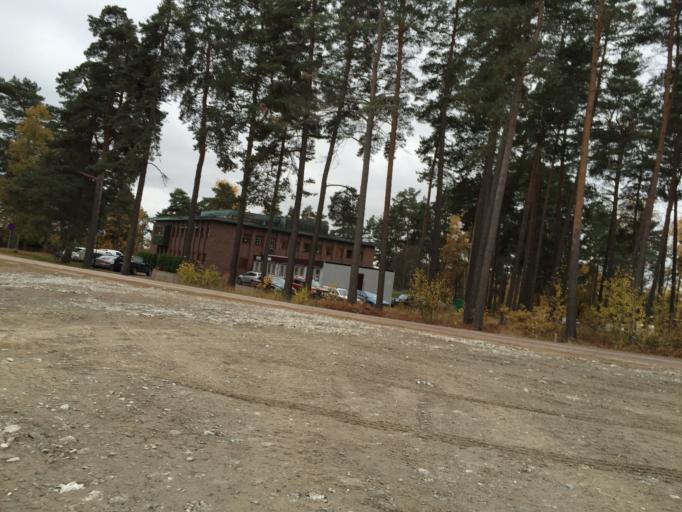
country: SE
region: Vaestmanland
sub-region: Hallstahammars Kommun
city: Hallstahammar
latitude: 59.6232
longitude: 16.2108
